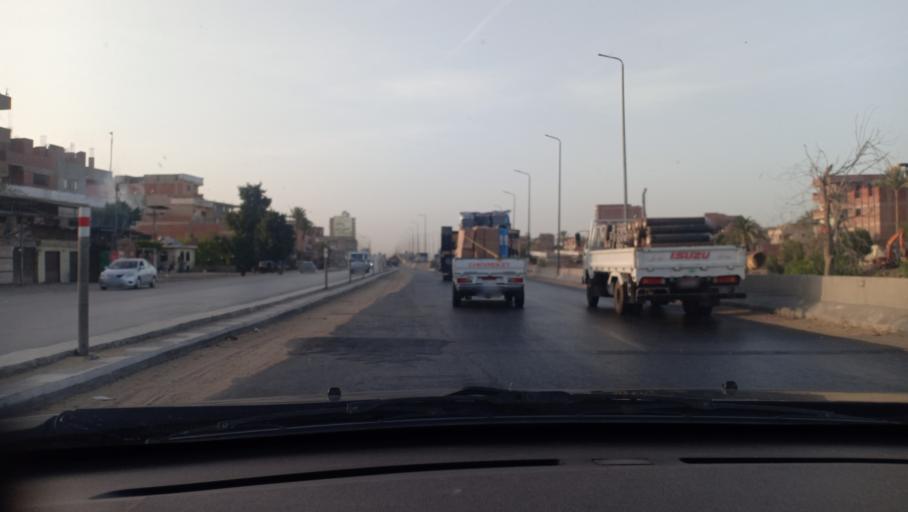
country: EG
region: Muhafazat al Minufiyah
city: Quwaysina
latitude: 30.5442
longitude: 31.2692
